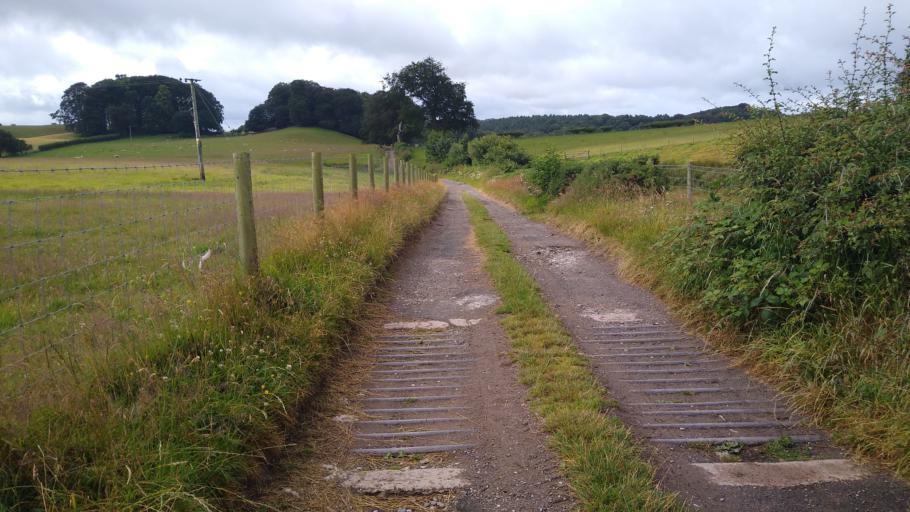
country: GB
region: England
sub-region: Cumbria
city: Brampton
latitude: 54.9286
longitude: -2.7325
